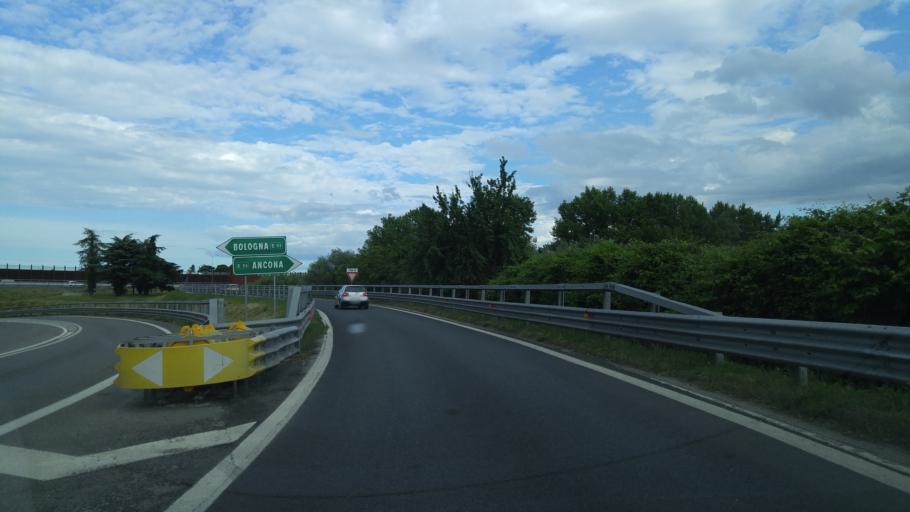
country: IT
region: Emilia-Romagna
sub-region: Provincia di Rimini
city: Rimini
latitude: 44.0354
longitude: 12.5670
